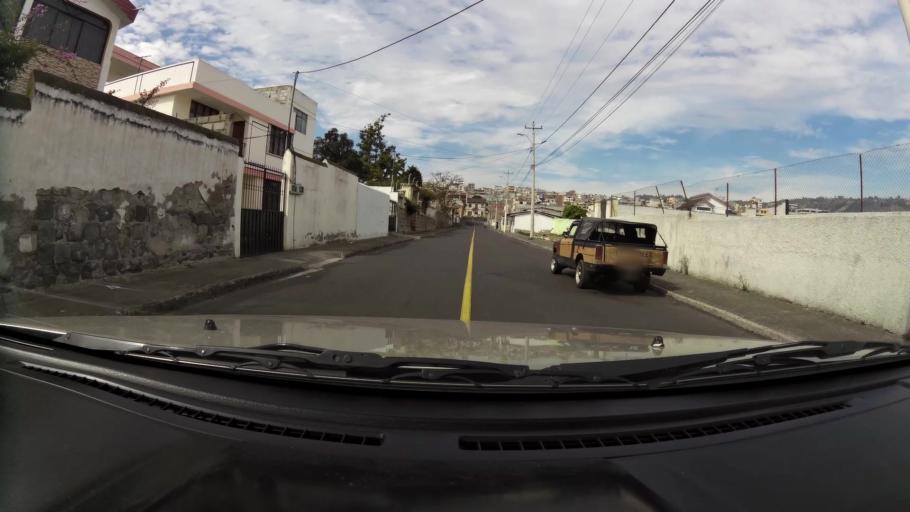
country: EC
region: Tungurahua
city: Ambato
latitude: -1.2500
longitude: -78.6296
